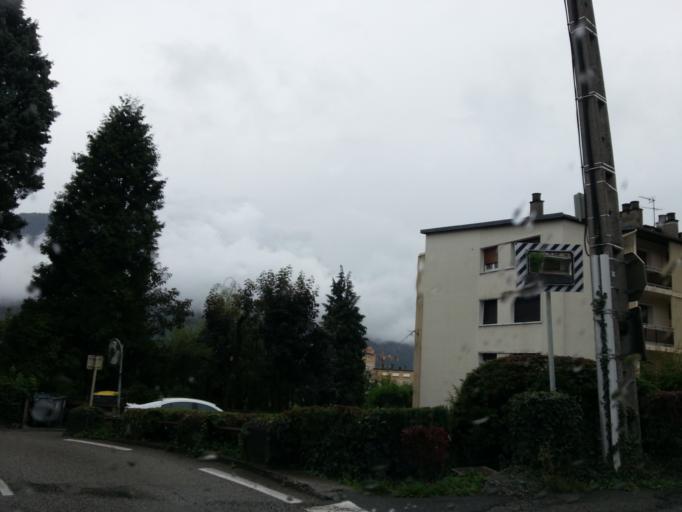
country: FR
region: Rhone-Alpes
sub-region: Departement de la Savoie
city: Albertville
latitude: 45.6791
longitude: 6.3891
